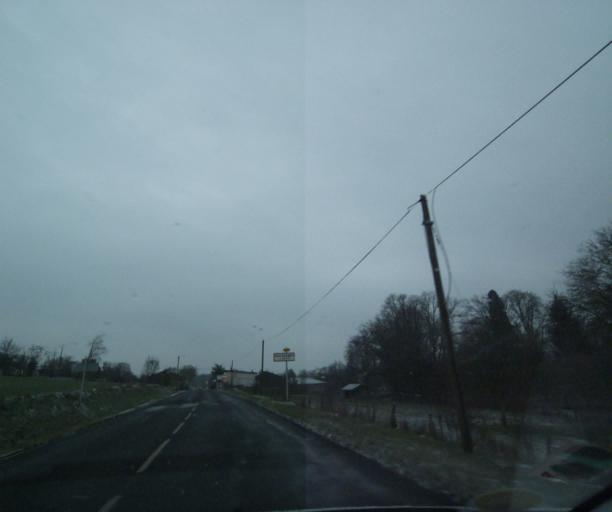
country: FR
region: Champagne-Ardenne
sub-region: Departement de la Haute-Marne
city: Wassy
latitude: 48.4488
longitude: 4.9574
